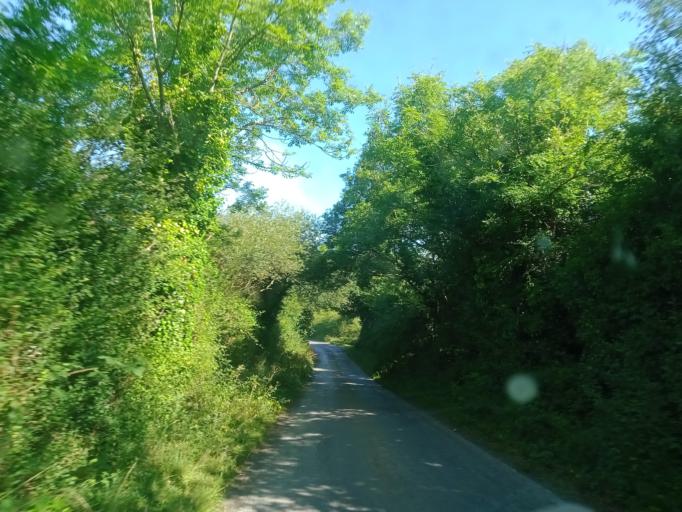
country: IE
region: Leinster
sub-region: Kilkenny
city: Ballyragget
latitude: 52.7888
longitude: -7.4227
